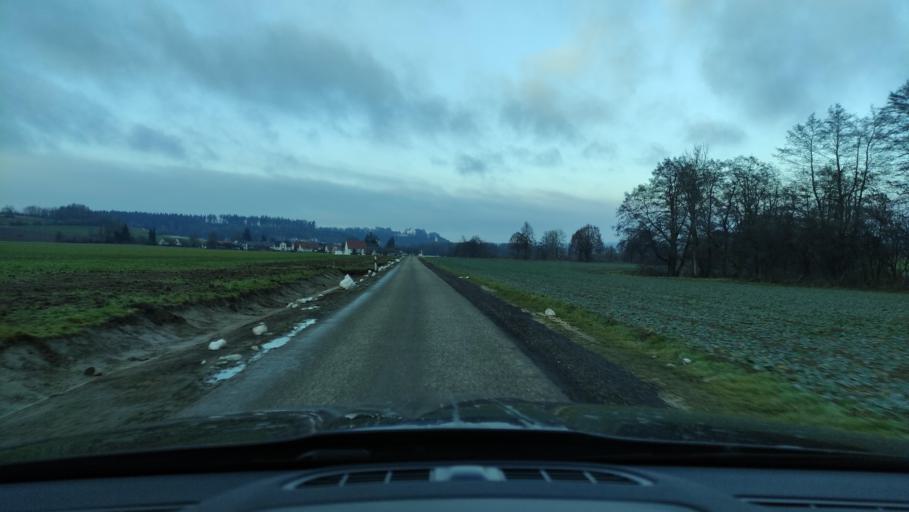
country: DE
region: Bavaria
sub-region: Swabia
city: Deisenhausen
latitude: 48.2870
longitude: 10.3573
